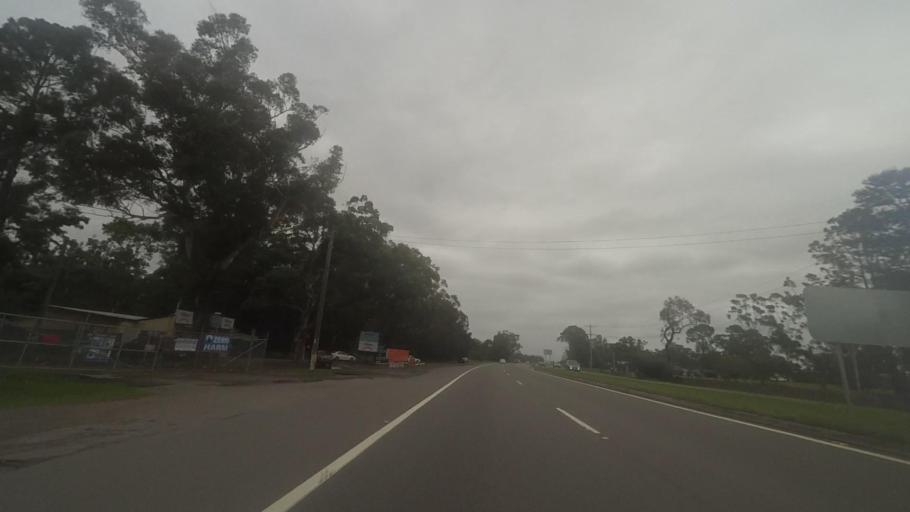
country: AU
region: New South Wales
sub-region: Port Stephens Shire
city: Raymond Terrace
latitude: -32.7942
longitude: 151.7228
